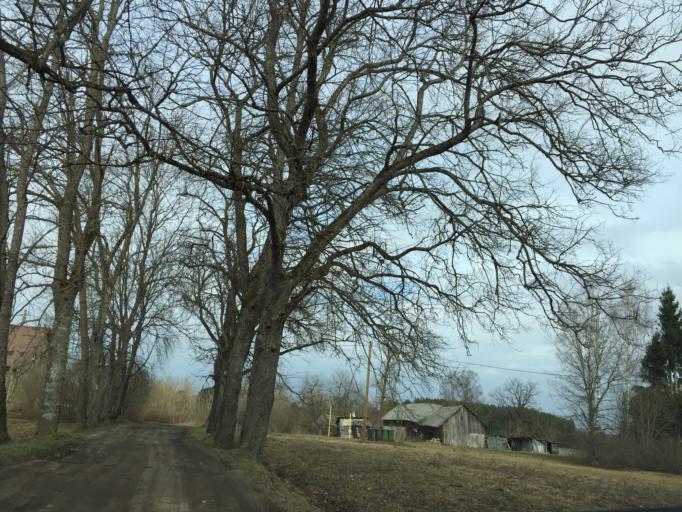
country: LV
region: Garkalne
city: Garkalne
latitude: 57.0754
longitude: 24.4405
